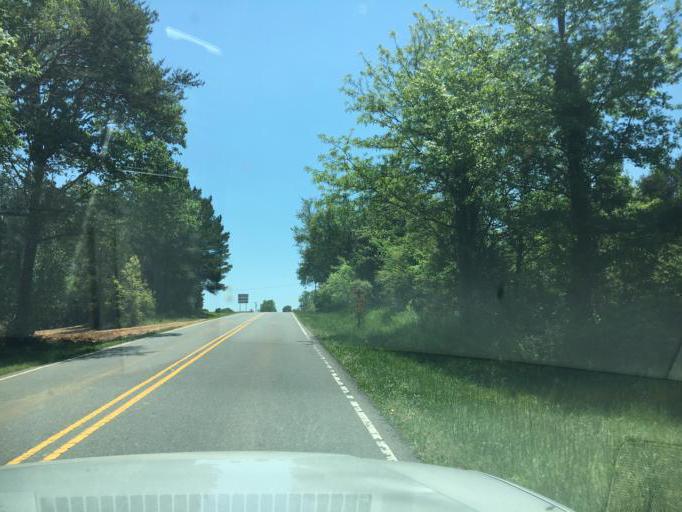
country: US
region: South Carolina
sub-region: Cherokee County
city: Blacksburg
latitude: 35.1828
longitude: -81.5709
